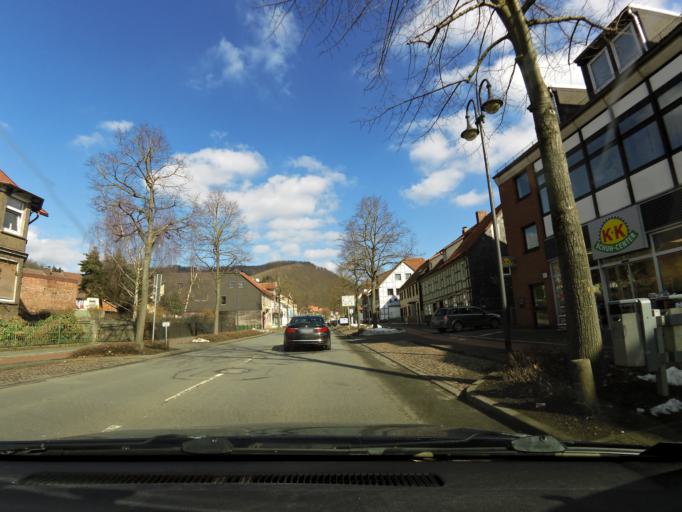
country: DE
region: Lower Saxony
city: Bad Lauterberg im Harz
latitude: 51.6277
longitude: 10.4667
